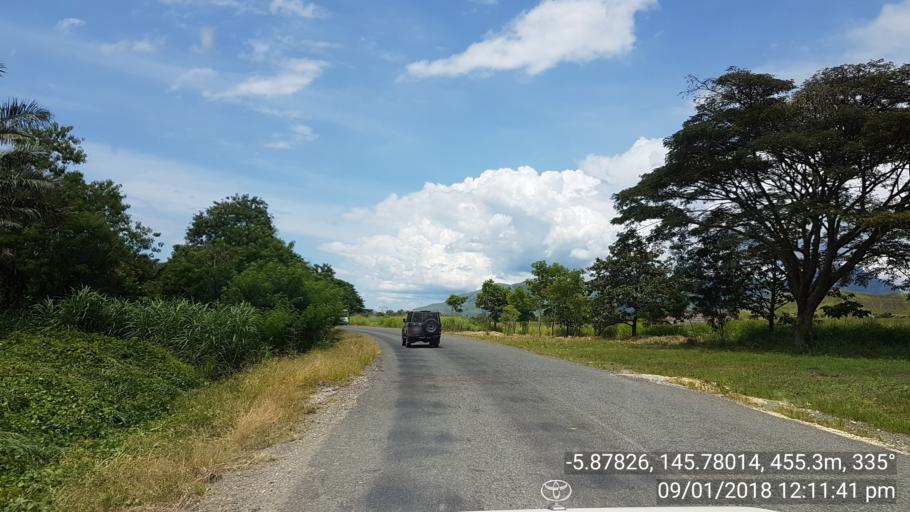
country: PG
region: Eastern Highlands
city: Kainantu
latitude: -5.8784
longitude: 145.7802
